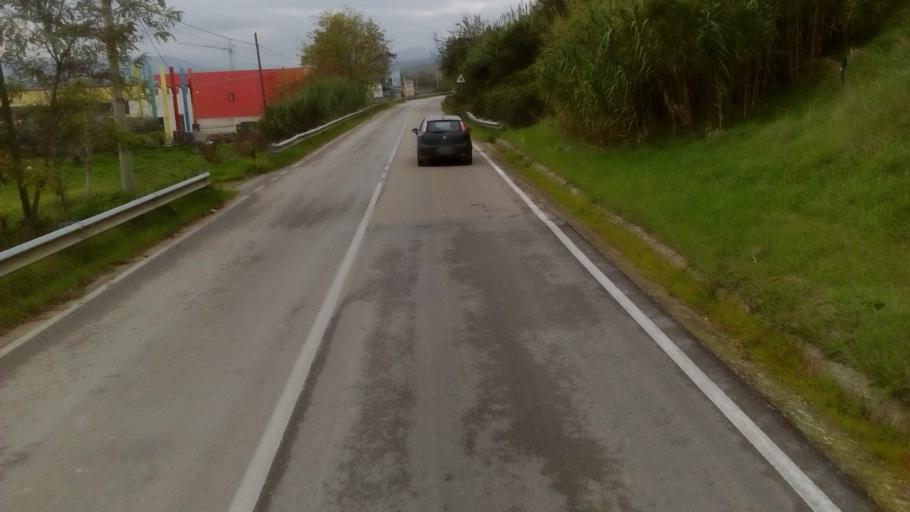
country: IT
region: Abruzzo
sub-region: Provincia di Chieti
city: San Salvo
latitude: 42.0293
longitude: 14.7397
